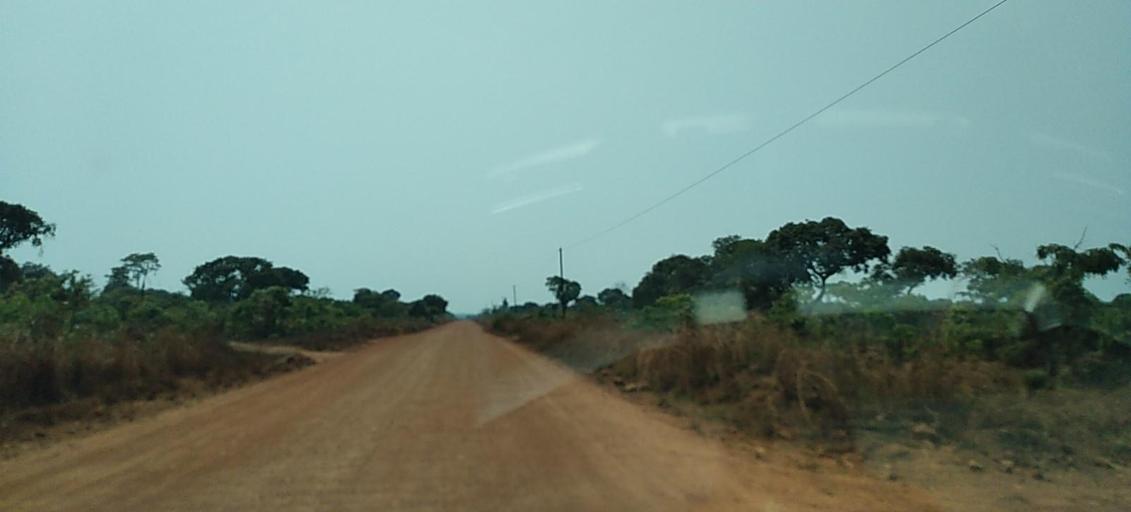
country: ZM
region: North-Western
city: Kansanshi
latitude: -11.9967
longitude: 26.6001
